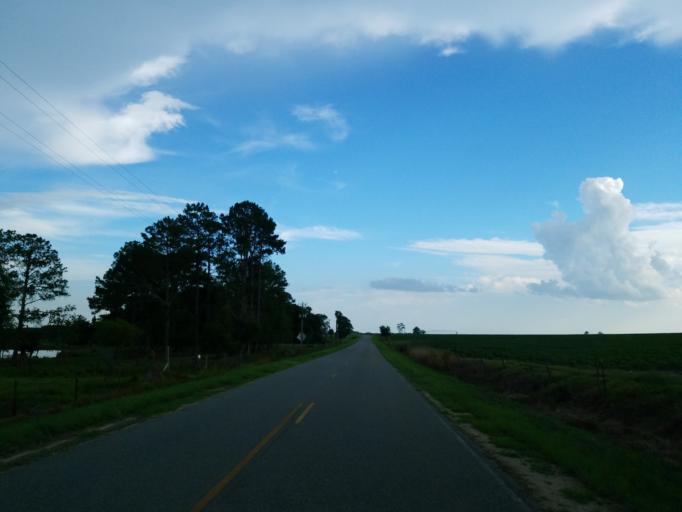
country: US
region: Georgia
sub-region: Tift County
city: Omega
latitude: 31.2722
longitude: -83.5189
